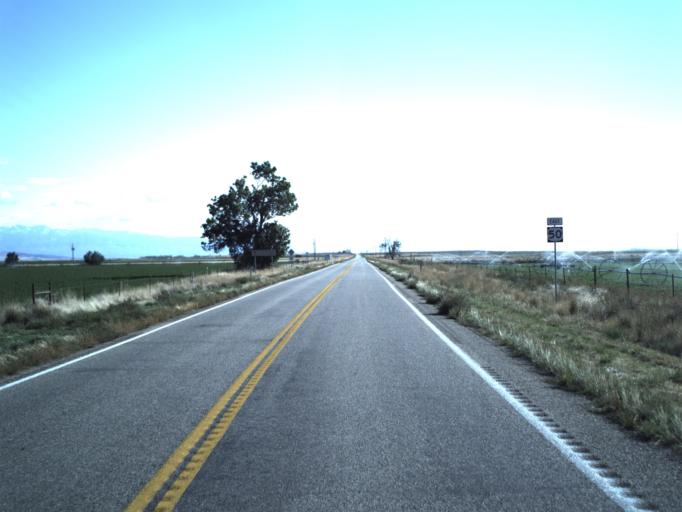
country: US
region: Utah
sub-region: Millard County
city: Delta
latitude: 39.2029
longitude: -112.4099
